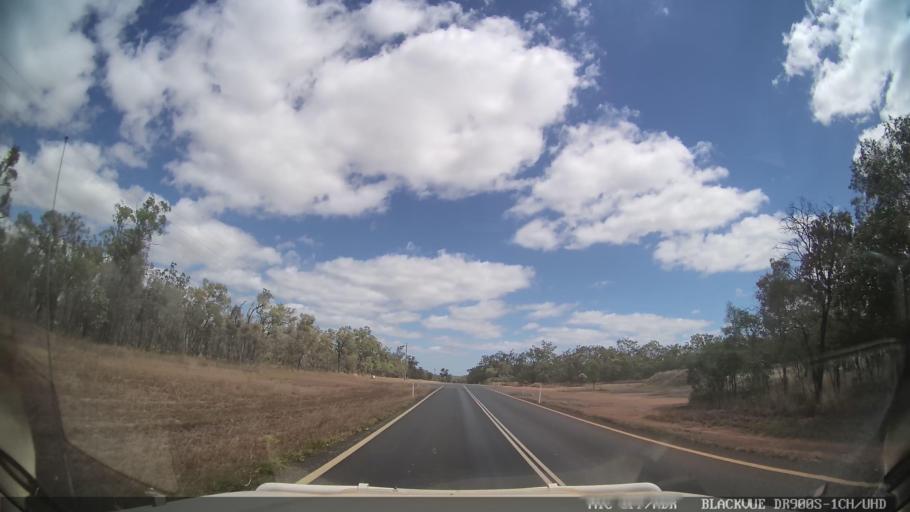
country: AU
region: Queensland
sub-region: Tablelands
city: Ravenshoe
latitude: -17.9104
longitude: 144.8801
